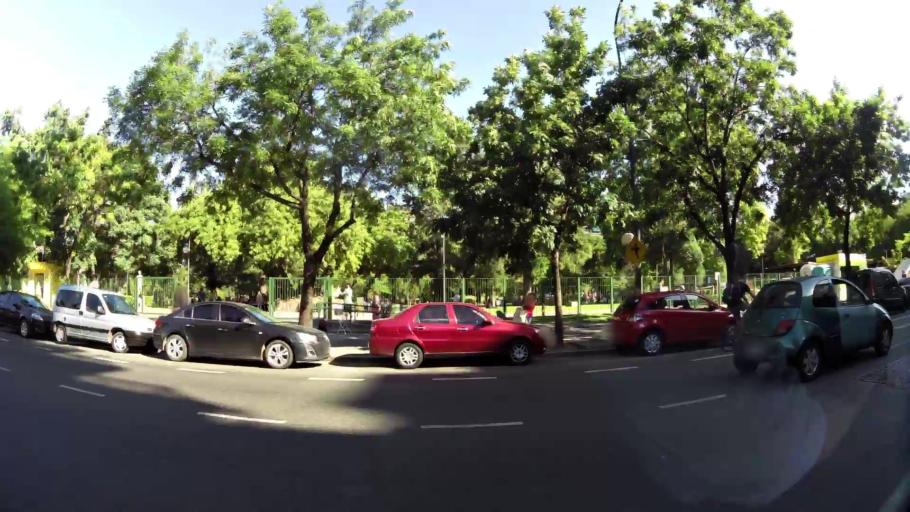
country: AR
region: Buenos Aires F.D.
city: Colegiales
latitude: -34.6174
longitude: -58.4345
